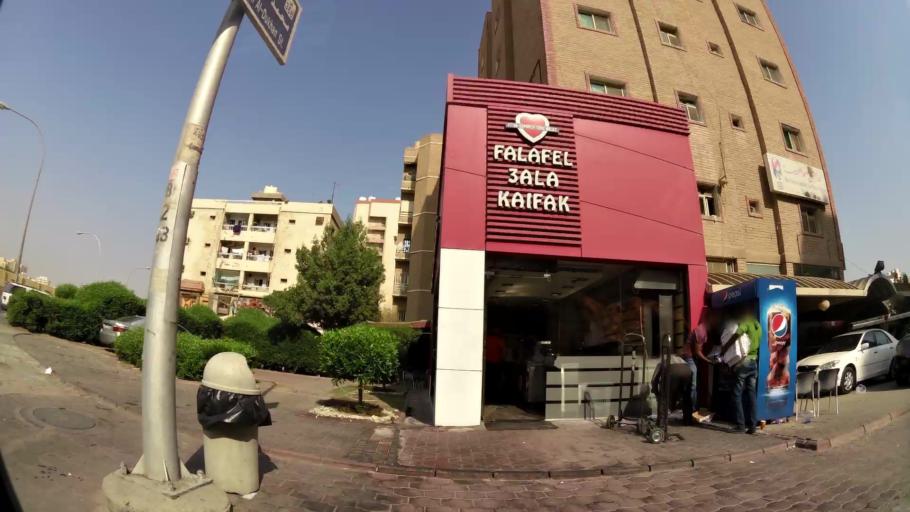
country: KW
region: Muhafazat Hawalli
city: Hawalli
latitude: 29.3321
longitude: 48.0156
